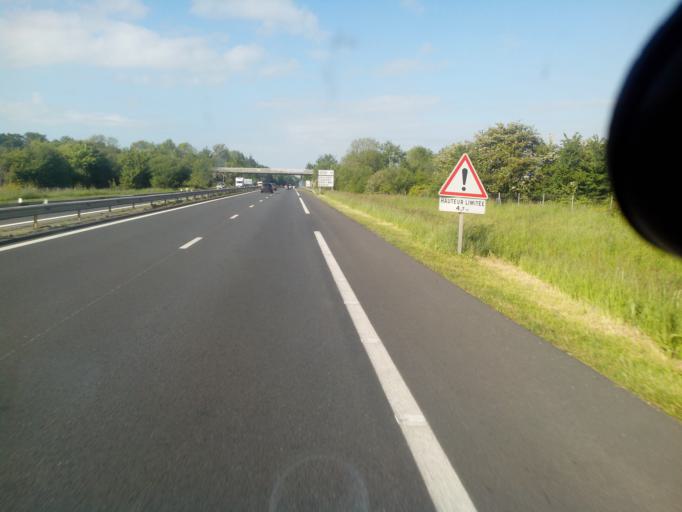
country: FR
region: Lower Normandy
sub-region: Departement du Calvados
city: Troarn
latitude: 49.1868
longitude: -0.1932
